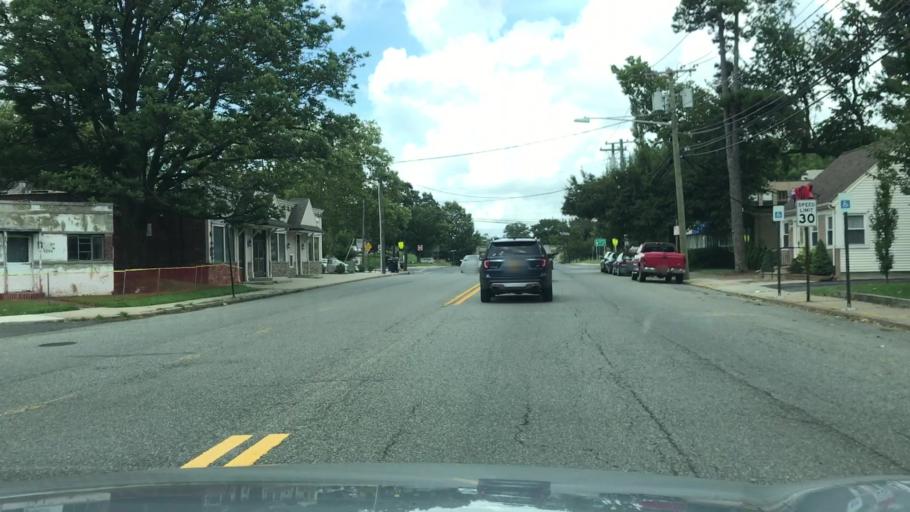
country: US
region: New Jersey
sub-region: Bergen County
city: Teaneck
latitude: 40.8887
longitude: -74.0048
